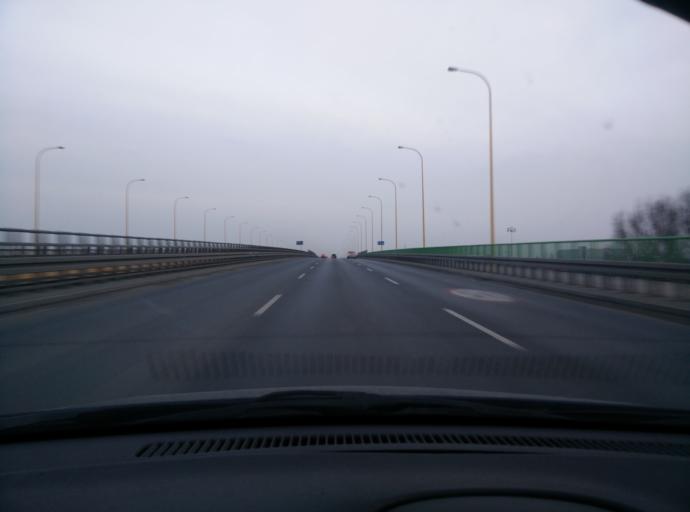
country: PL
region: Greater Poland Voivodeship
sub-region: Poznan
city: Poznan
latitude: 52.3742
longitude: 16.9845
